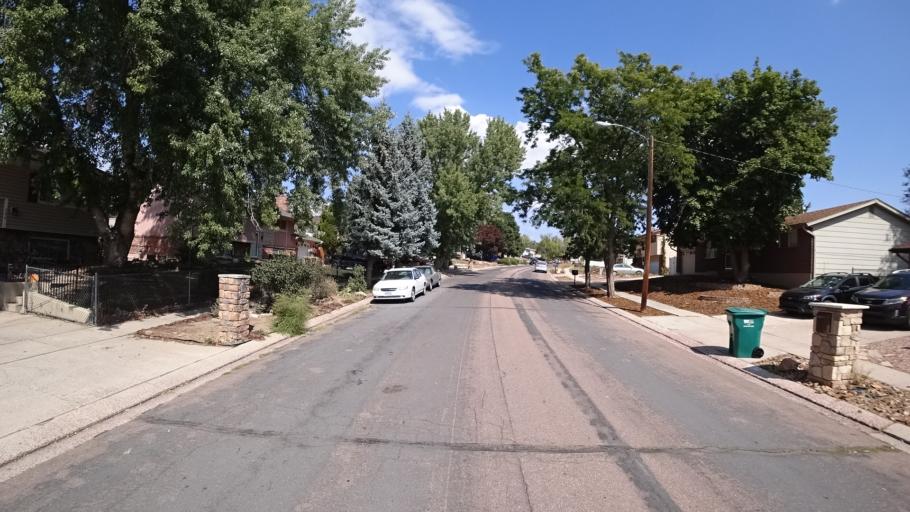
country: US
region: Colorado
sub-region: El Paso County
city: Stratmoor
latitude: 38.8271
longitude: -104.7659
